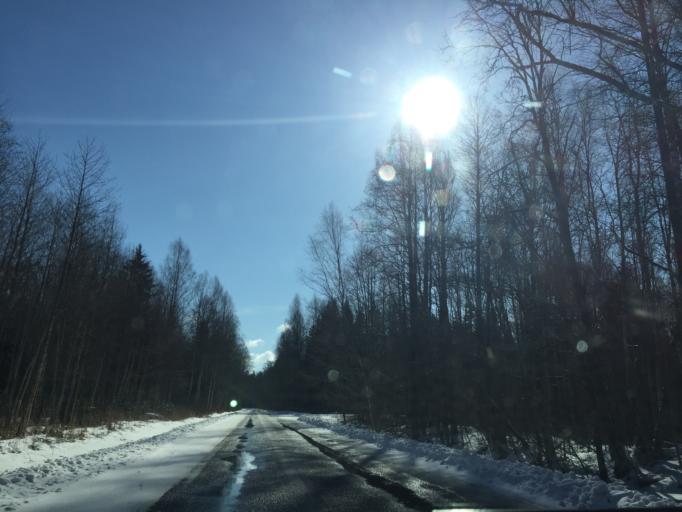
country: LV
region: Salacgrivas
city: Ainazi
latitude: 57.9988
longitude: 24.5308
